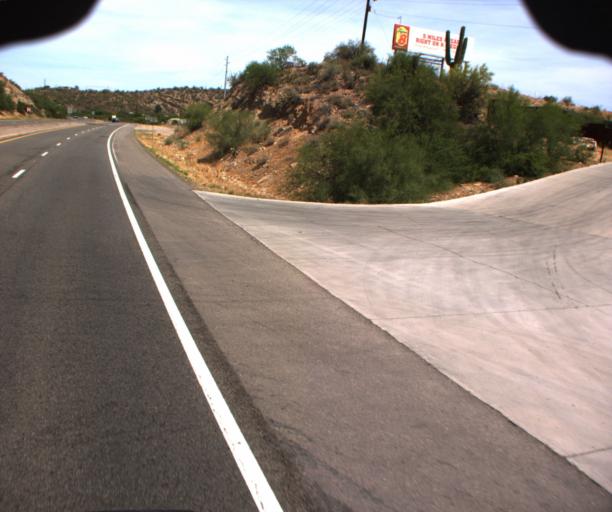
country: US
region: Arizona
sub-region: Maricopa County
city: Wickenburg
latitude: 33.9139
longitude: -112.6764
